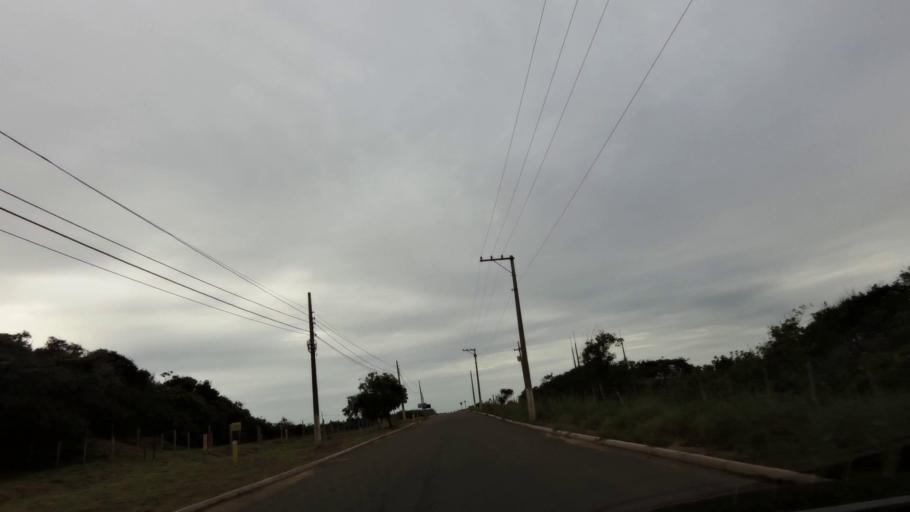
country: BR
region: Espirito Santo
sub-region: Piuma
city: Piuma
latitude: -20.7998
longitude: -40.5849
